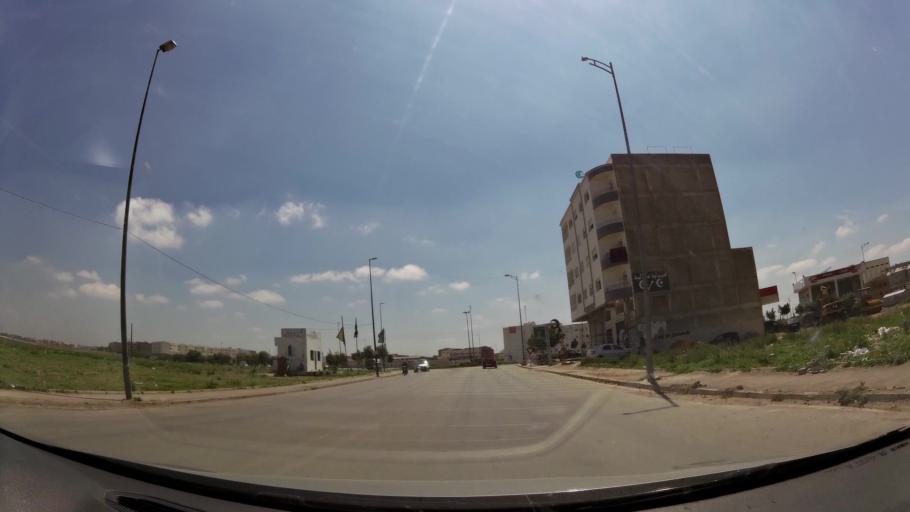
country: MA
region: Fes-Boulemane
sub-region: Fes
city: Fes
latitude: 34.0097
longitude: -5.0452
